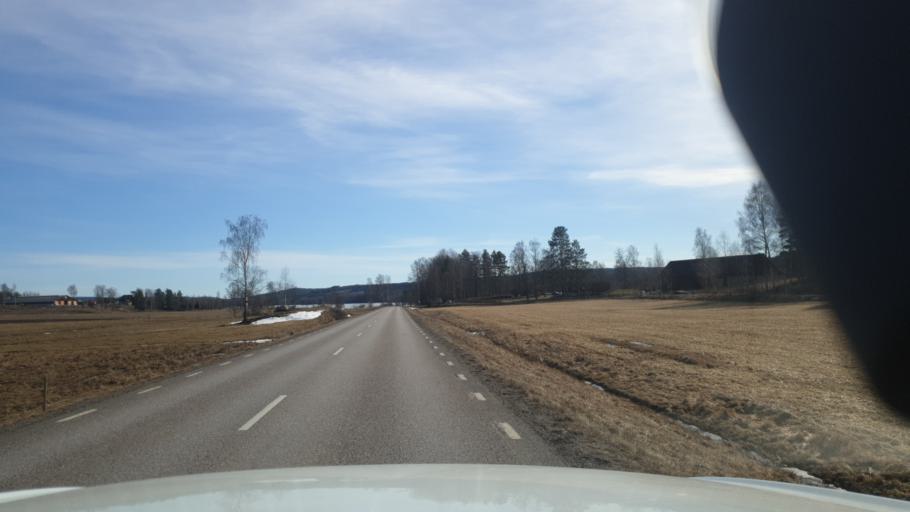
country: SE
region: Vaermland
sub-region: Arvika Kommun
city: Arvika
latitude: 59.5016
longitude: 12.6816
